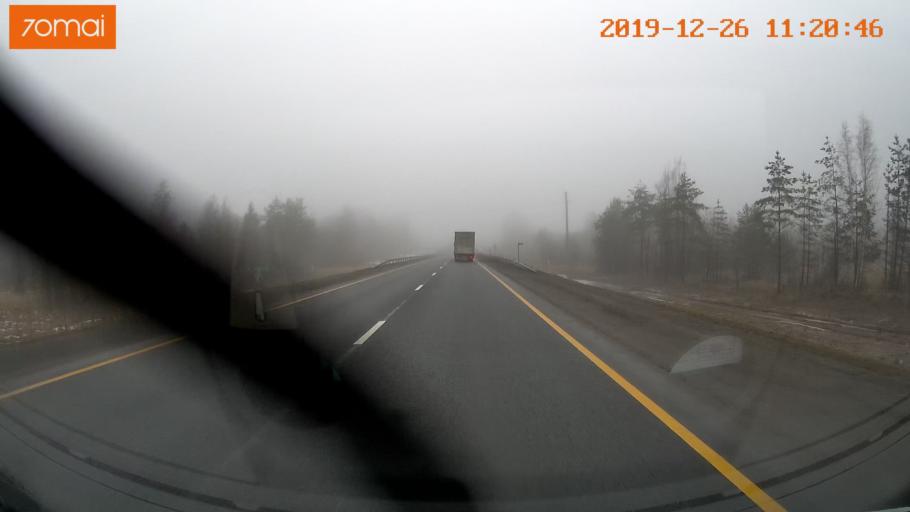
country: RU
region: Vologda
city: Chebsara
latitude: 59.1207
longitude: 38.9815
